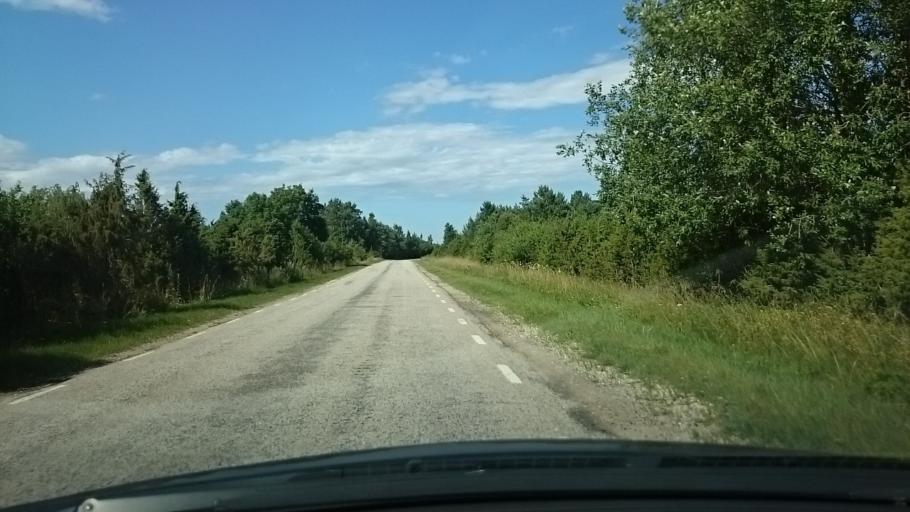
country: EE
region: Laeaene
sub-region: Haapsalu linn
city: Haapsalu
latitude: 59.1136
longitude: 23.5327
